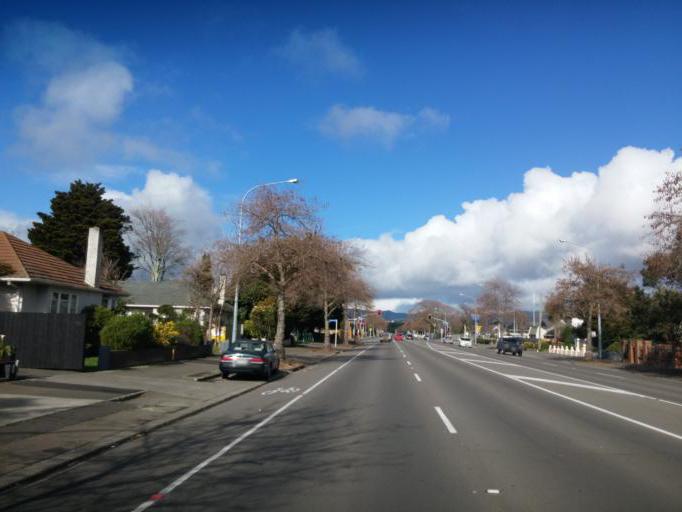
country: NZ
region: Manawatu-Wanganui
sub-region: Palmerston North City
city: Palmerston North
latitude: -40.3638
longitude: 175.6171
